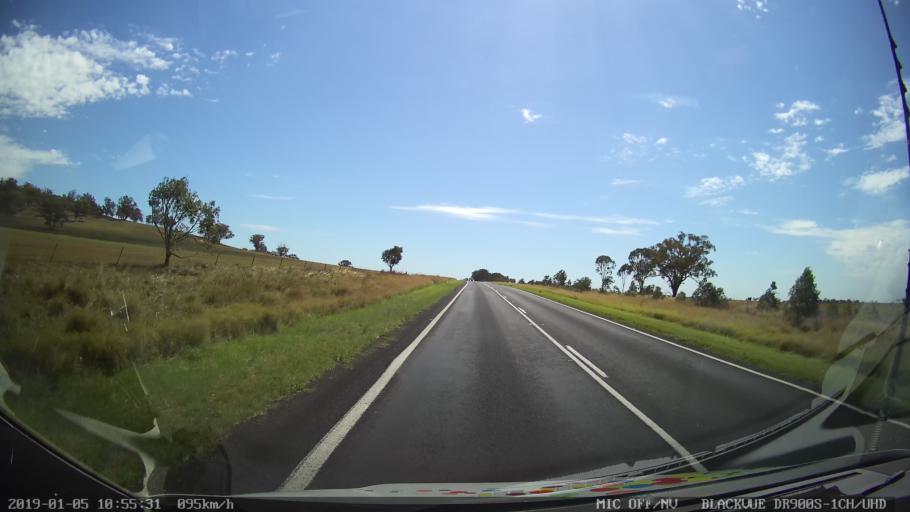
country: AU
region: New South Wales
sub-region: Warrumbungle Shire
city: Coonabarabran
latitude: -31.4479
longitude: 149.1451
